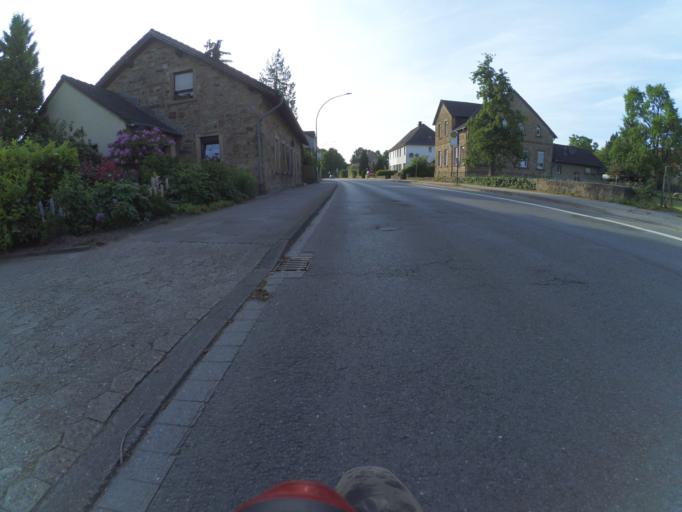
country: DE
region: North Rhine-Westphalia
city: Ibbenburen
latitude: 52.2708
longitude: 7.7207
